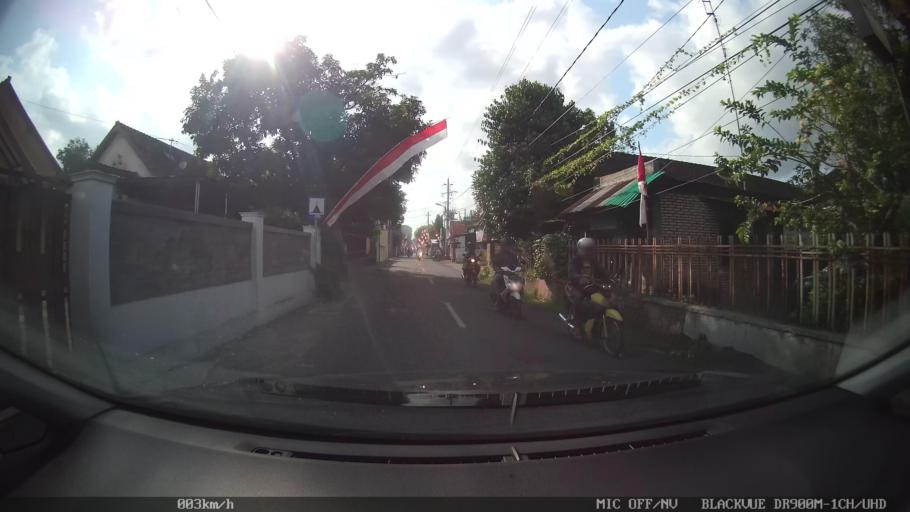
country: ID
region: Daerah Istimewa Yogyakarta
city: Kasihan
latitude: -7.8174
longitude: 110.3579
